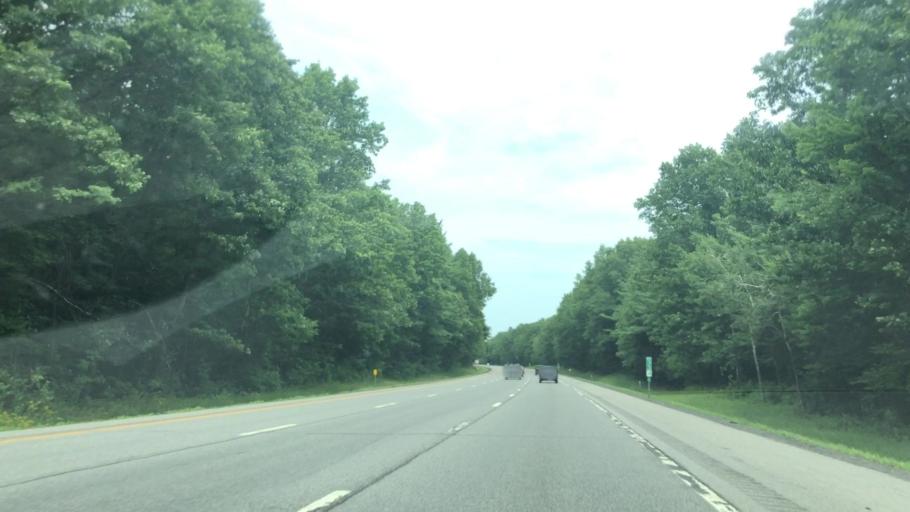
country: US
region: New York
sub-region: Saratoga County
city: Saratoga Springs
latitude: 43.1342
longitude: -73.7321
